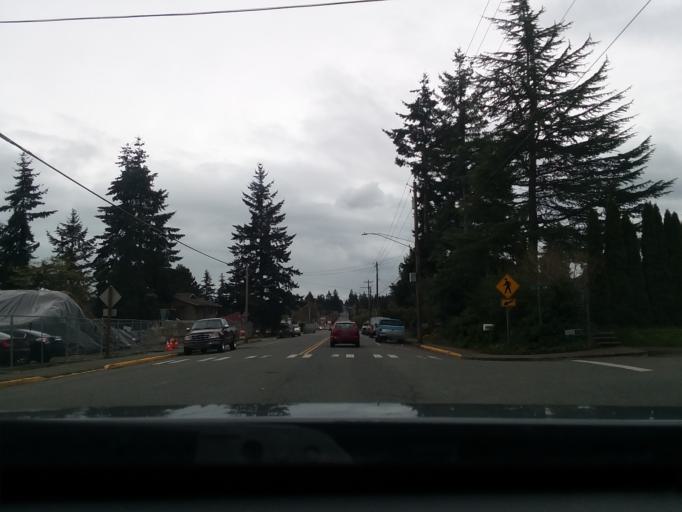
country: US
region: Washington
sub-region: Snohomish County
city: Esperance
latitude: 47.7980
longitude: -122.3356
